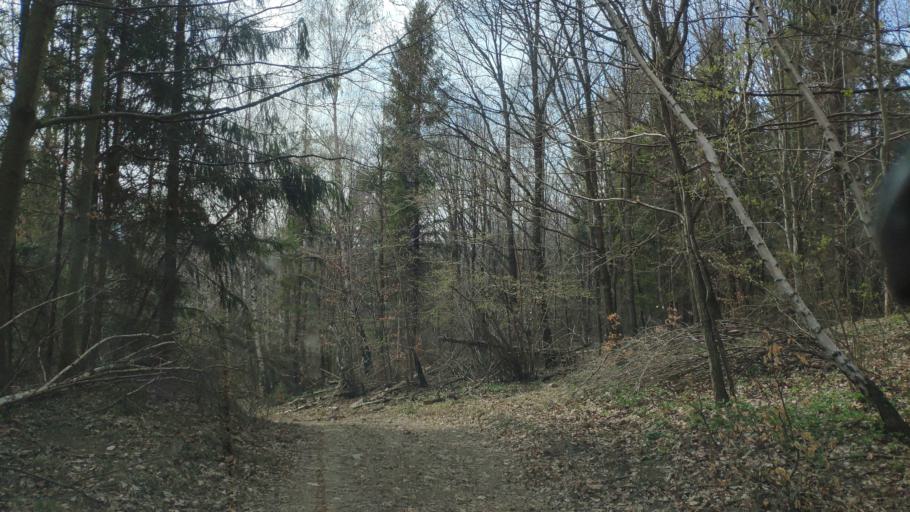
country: SK
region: Kosicky
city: Moldava nad Bodvou
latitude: 48.7433
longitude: 21.0361
